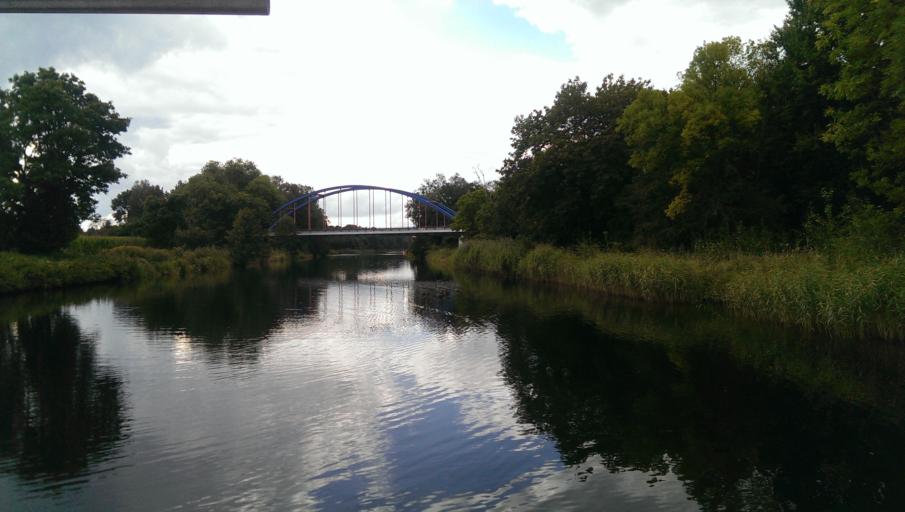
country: DE
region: Brandenburg
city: Marienwerder
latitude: 52.8467
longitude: 13.5473
